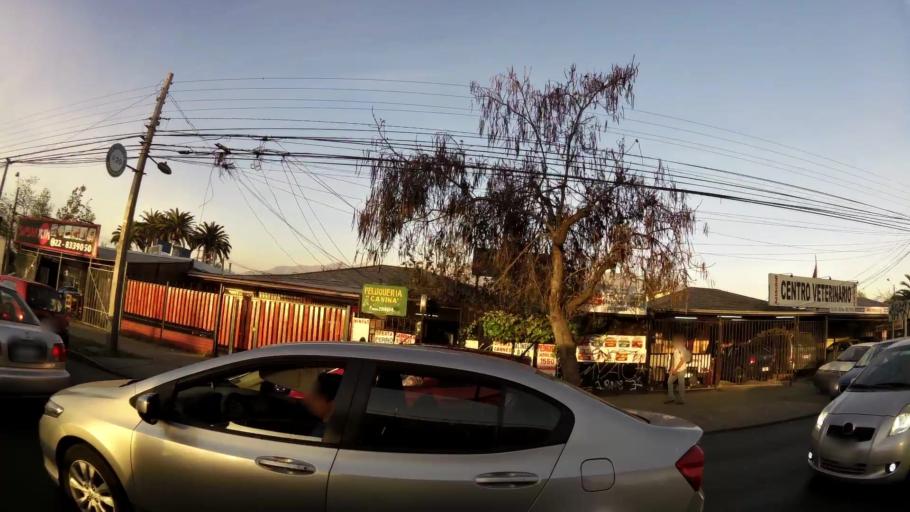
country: CL
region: Santiago Metropolitan
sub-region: Provincia de Santiago
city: La Pintana
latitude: -33.5439
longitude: -70.5890
